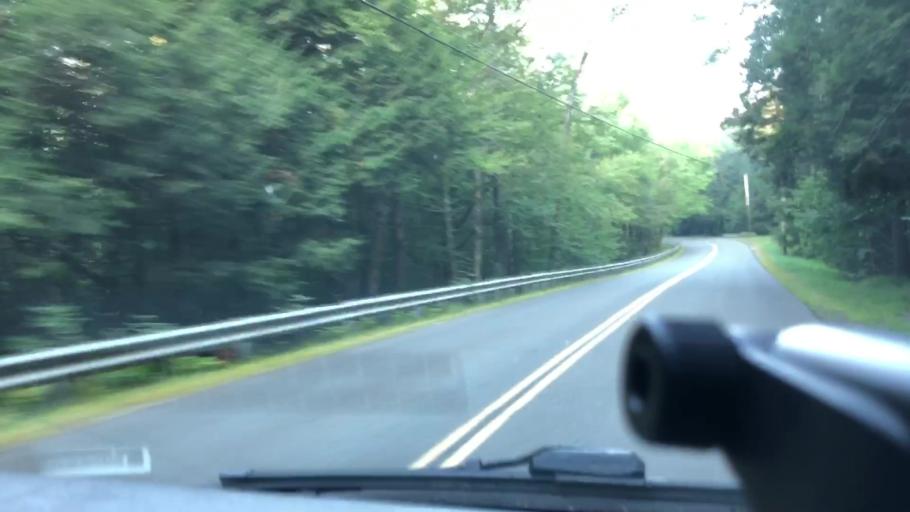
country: US
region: Massachusetts
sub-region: Franklin County
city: Ashfield
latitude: 42.4946
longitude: -72.8627
